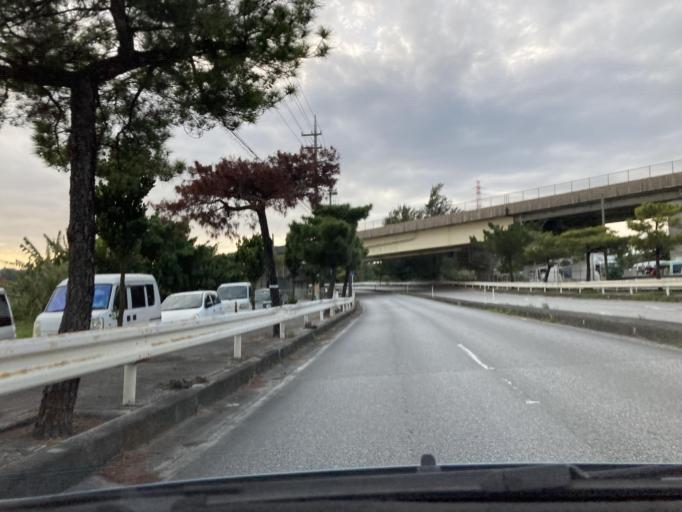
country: JP
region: Okinawa
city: Ishikawa
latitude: 26.4359
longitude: 127.8240
